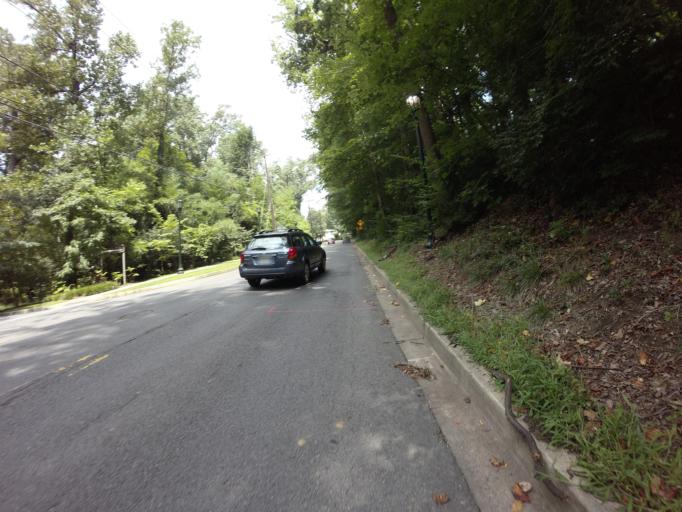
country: US
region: Maryland
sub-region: Montgomery County
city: Kensington
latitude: 39.0326
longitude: -77.0882
